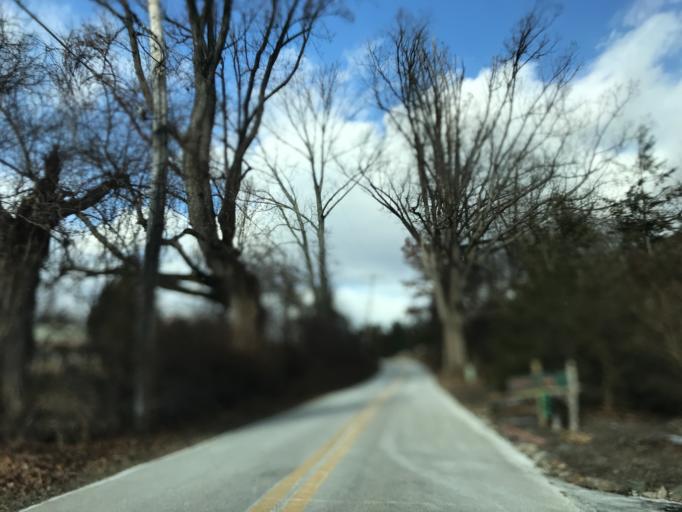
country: US
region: Maryland
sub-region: Baltimore County
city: Hunt Valley
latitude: 39.5846
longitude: -76.6546
